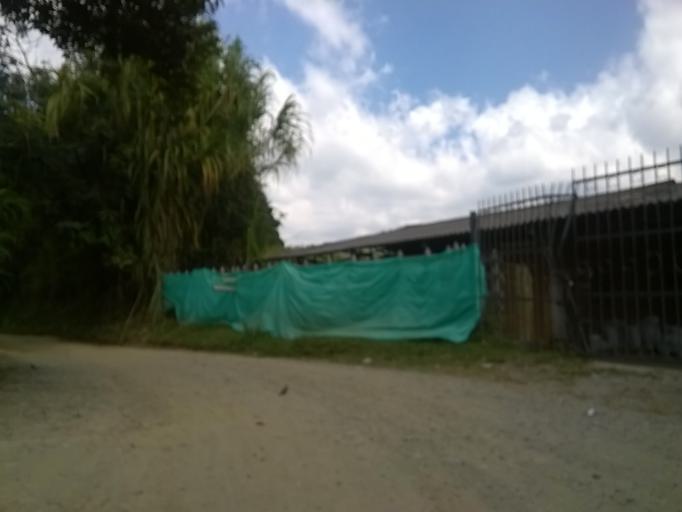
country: CO
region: Quindio
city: Circasia
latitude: 4.5907
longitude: -75.6307
